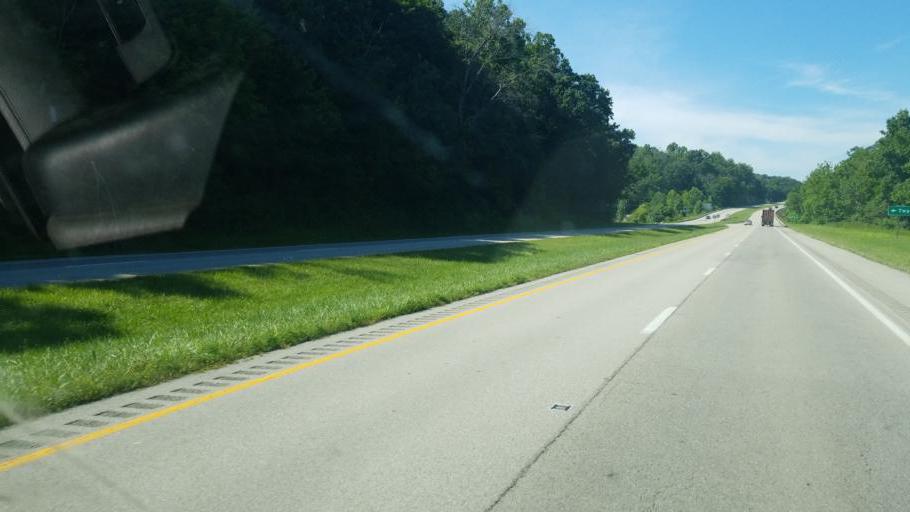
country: US
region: Ohio
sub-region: Meigs County
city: Pomeroy
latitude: 39.0708
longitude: -82.0189
